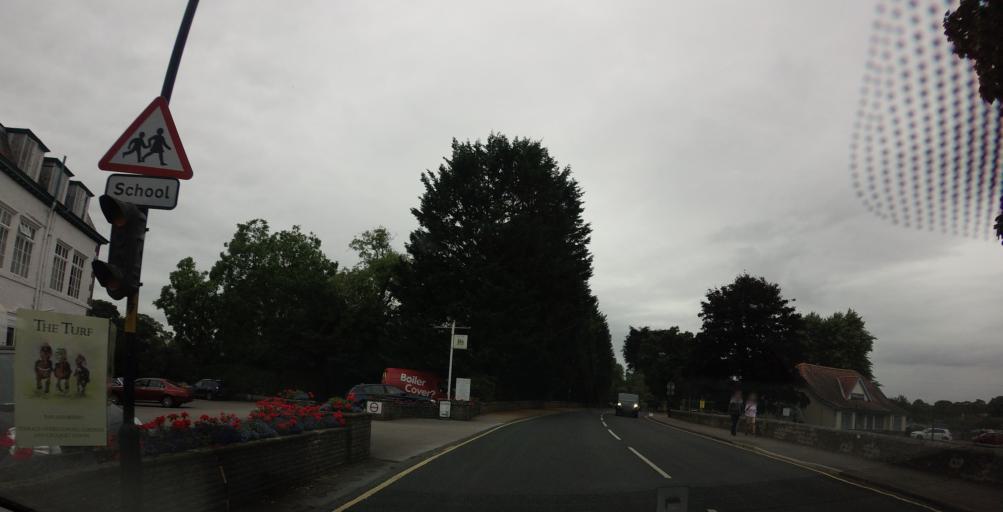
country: GB
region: England
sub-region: North Yorkshire
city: Ripon
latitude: 54.1360
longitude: -1.5302
